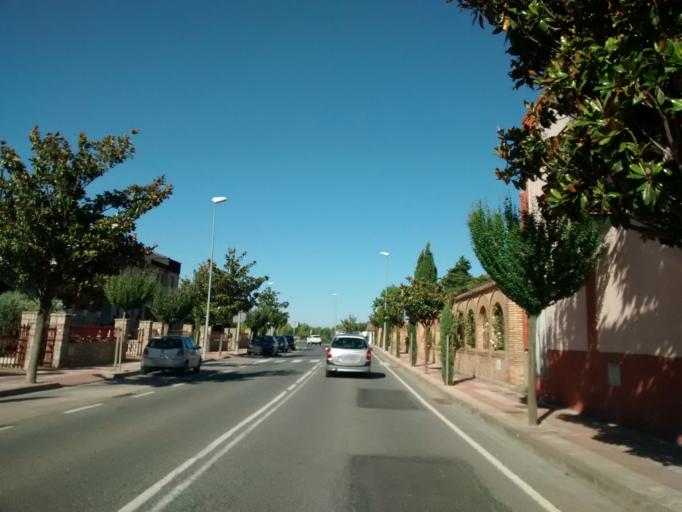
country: ES
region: Navarre
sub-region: Provincia de Navarra
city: Monteagudo
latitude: 41.9638
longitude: -1.6882
